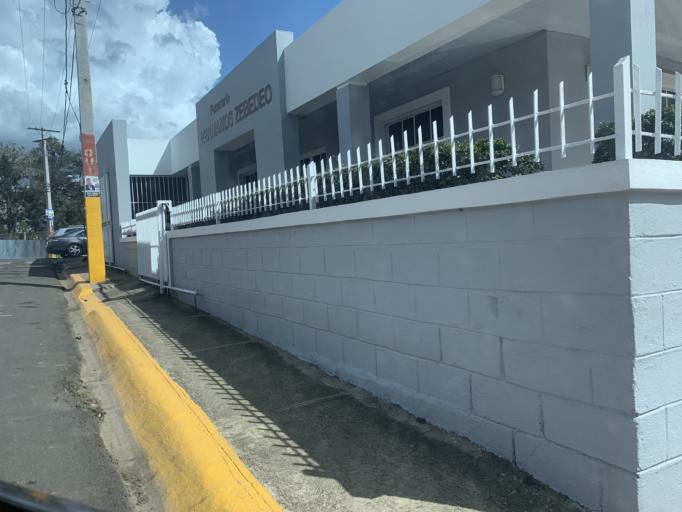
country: DO
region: Monte Plata
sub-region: Yamasa
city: Yamasa
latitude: 18.7677
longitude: -70.0243
